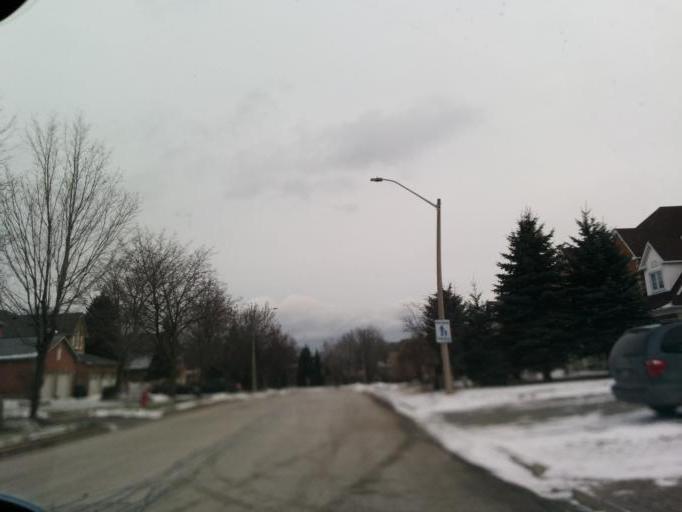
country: CA
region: Ontario
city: Mississauga
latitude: 43.5719
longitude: -79.6906
